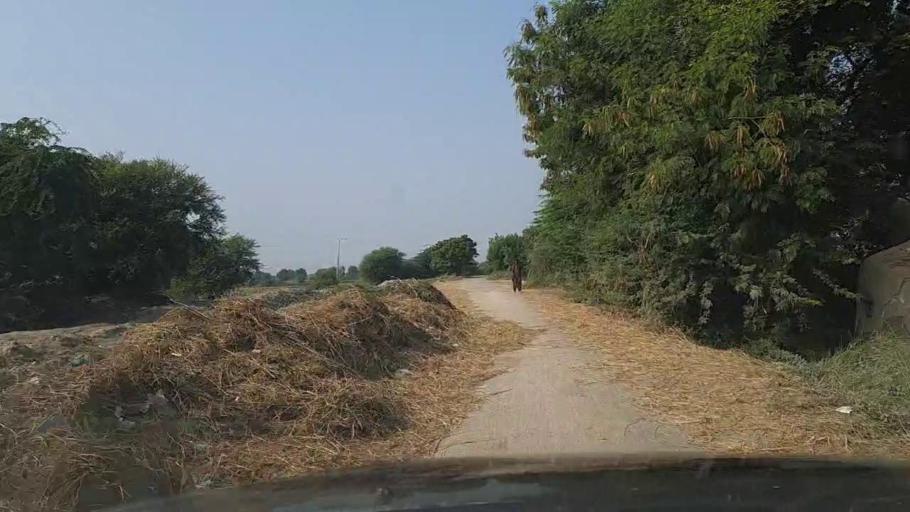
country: PK
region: Sindh
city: Mirpur Batoro
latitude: 24.7040
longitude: 68.2551
